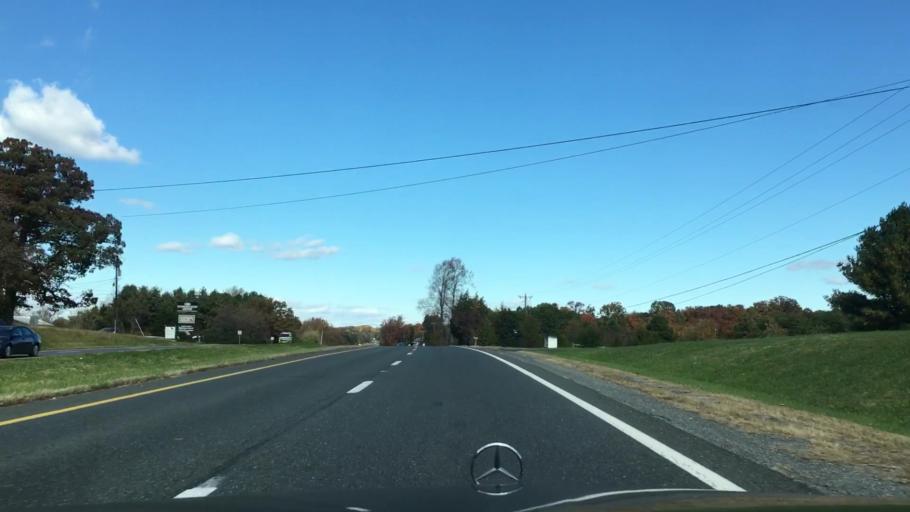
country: US
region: Virginia
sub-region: Campbell County
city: Altavista
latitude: 37.1855
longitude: -79.2038
